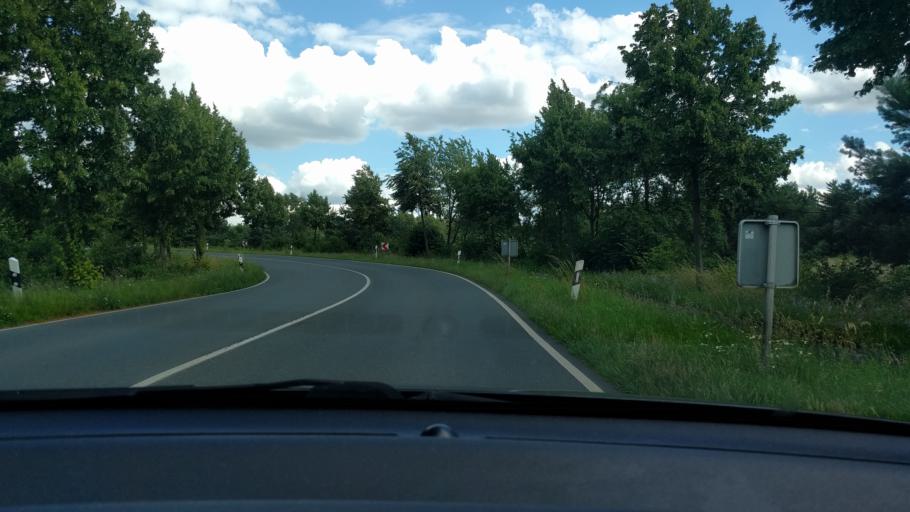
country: DE
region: North Rhine-Westphalia
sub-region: Regierungsbezirk Munster
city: Haltern
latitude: 51.7152
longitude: 7.2482
